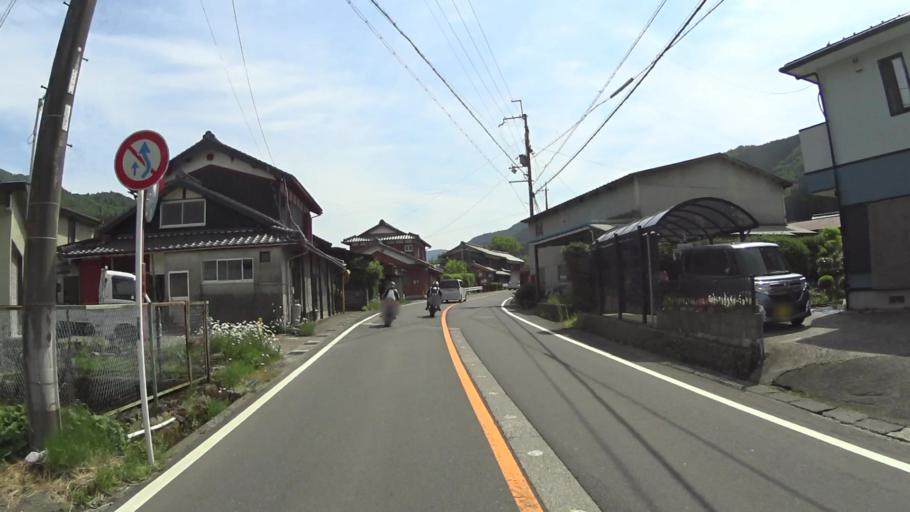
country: JP
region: Shiga Prefecture
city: Kitahama
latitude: 35.3423
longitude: 135.9082
